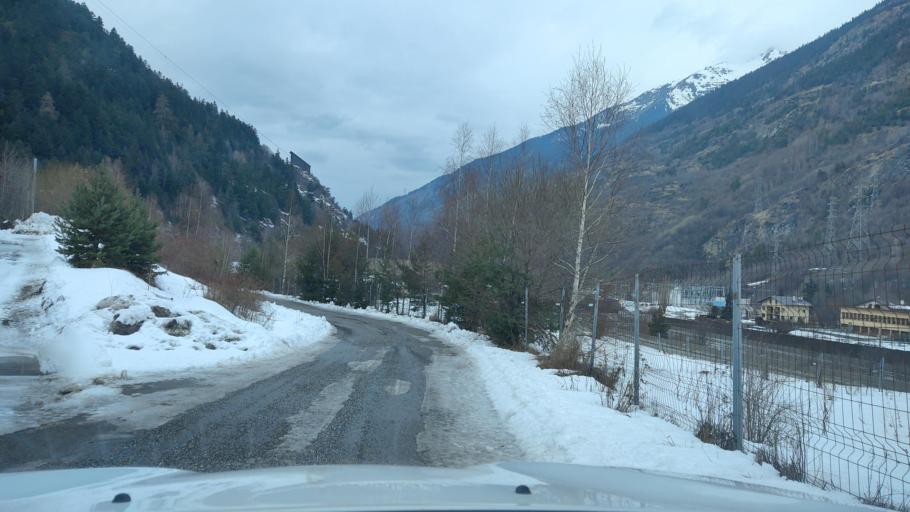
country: FR
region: Rhone-Alpes
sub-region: Departement de la Savoie
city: Modane
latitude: 45.2015
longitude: 6.5892
